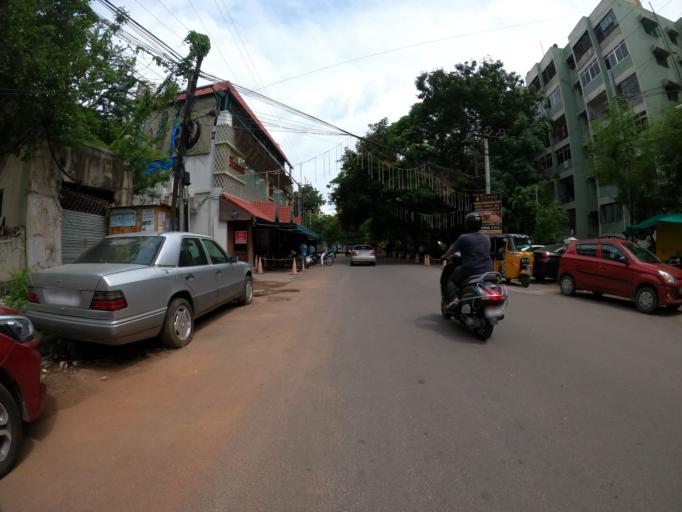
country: IN
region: Telangana
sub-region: Hyderabad
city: Hyderabad
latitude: 17.4003
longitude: 78.4589
